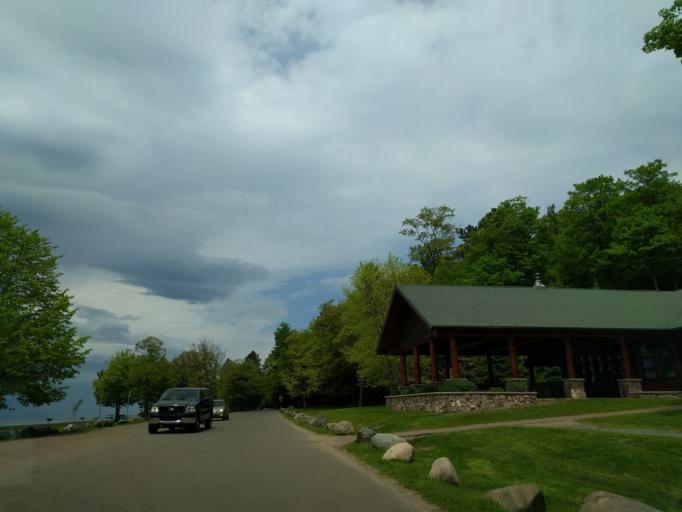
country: US
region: Michigan
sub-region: Marquette County
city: Marquette
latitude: 46.5864
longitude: -87.3851
